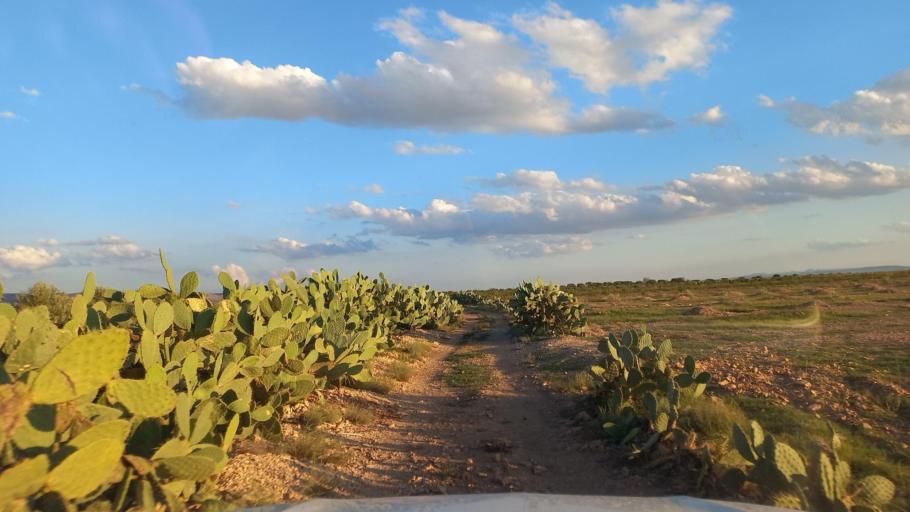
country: TN
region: Al Qasrayn
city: Sbiba
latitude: 35.3754
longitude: 9.0519
